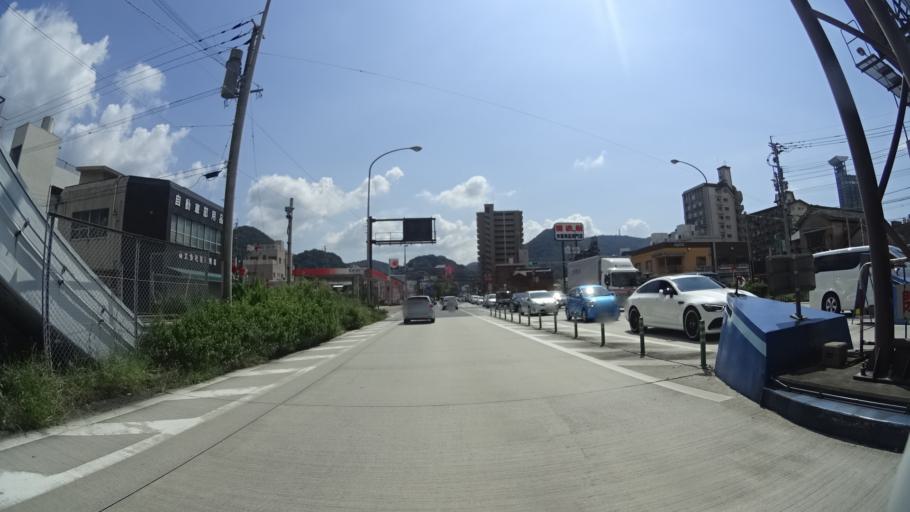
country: JP
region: Yamaguchi
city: Shimonoseki
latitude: 33.9506
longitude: 130.9690
